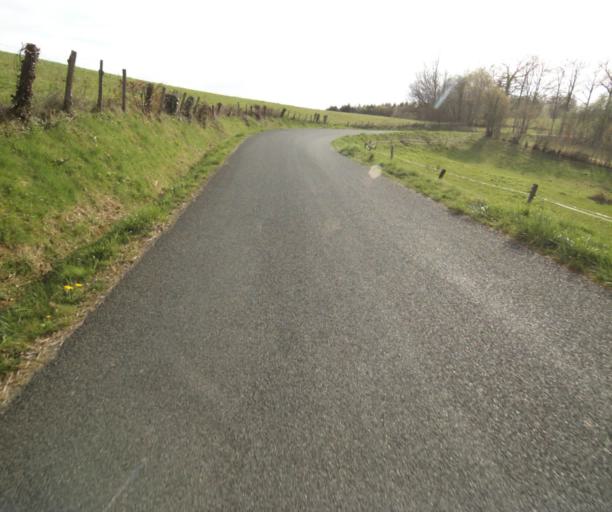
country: FR
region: Limousin
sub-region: Departement de la Correze
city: Naves
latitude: 45.2937
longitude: 1.7485
